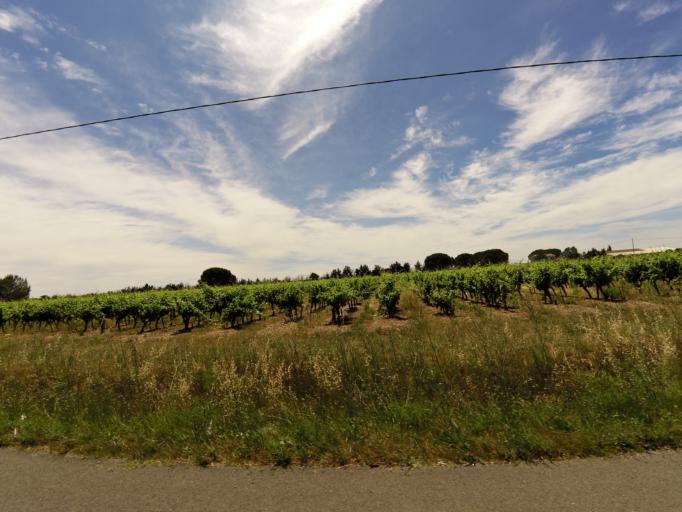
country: FR
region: Languedoc-Roussillon
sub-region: Departement du Gard
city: Aubord
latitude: 43.7718
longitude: 4.3300
